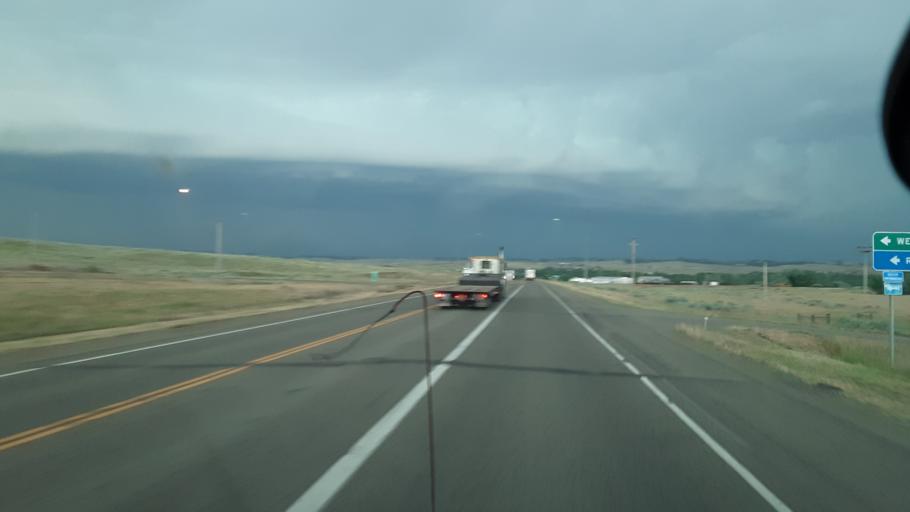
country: US
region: Montana
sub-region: Powder River County
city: Broadus
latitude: 45.4224
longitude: -105.3959
